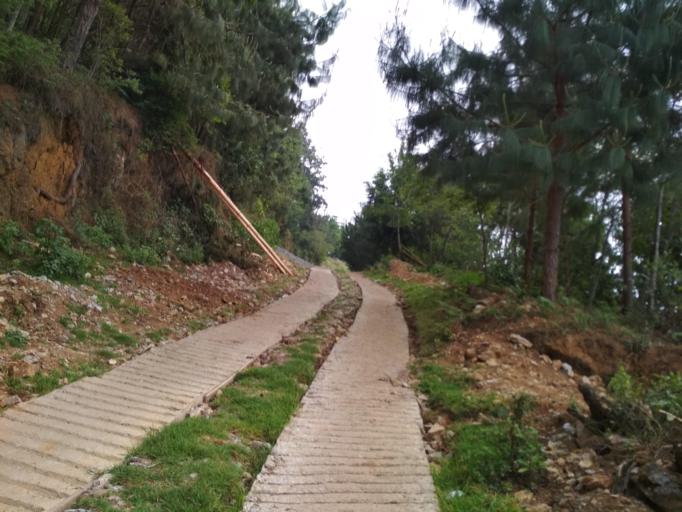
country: MX
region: Veracruz
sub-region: Camerino Z. Mendoza
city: Necoxtla
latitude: 18.7552
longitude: -97.1586
